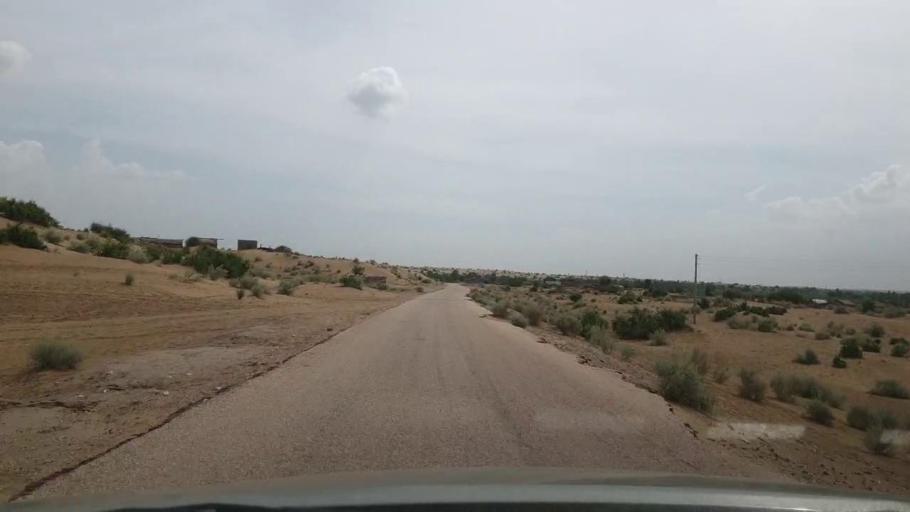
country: PK
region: Sindh
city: Kot Diji
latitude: 27.1684
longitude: 69.0384
